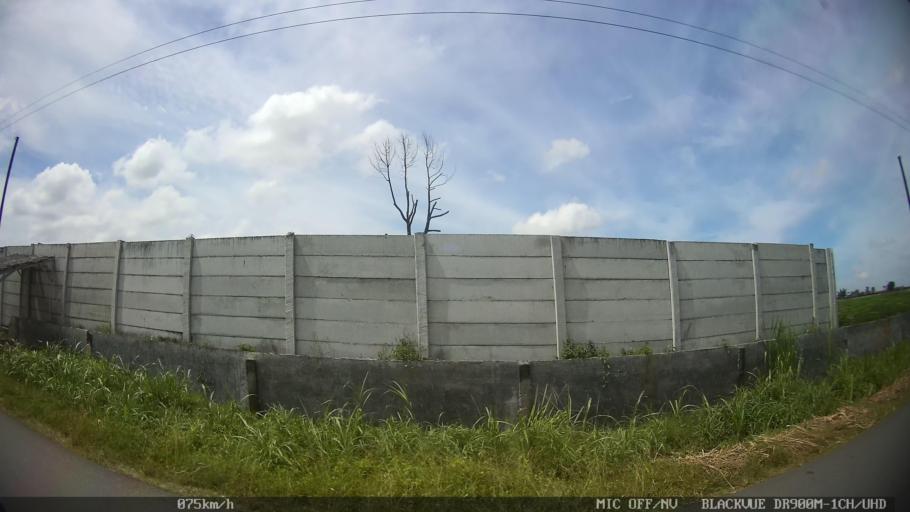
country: ID
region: North Sumatra
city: Percut
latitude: 3.5892
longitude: 98.8759
